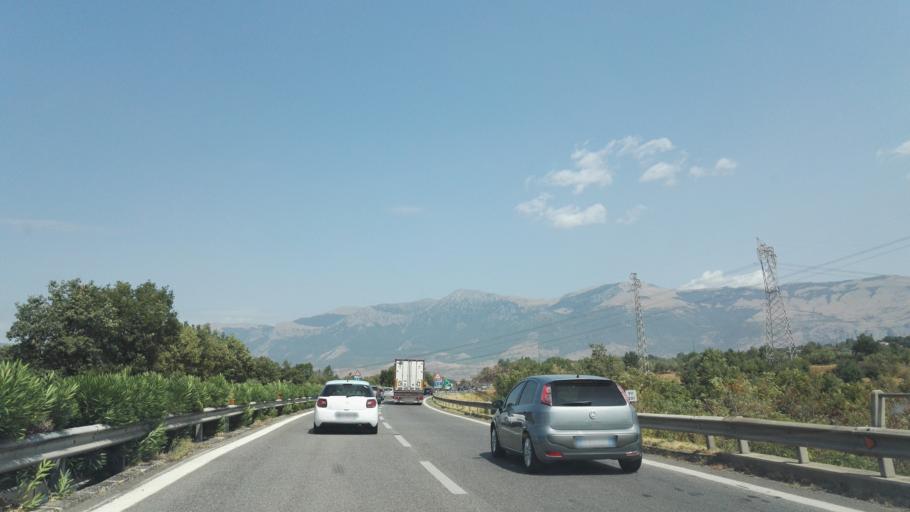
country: IT
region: Calabria
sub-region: Provincia di Cosenza
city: Castrovillari
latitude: 39.7756
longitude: 16.2232
